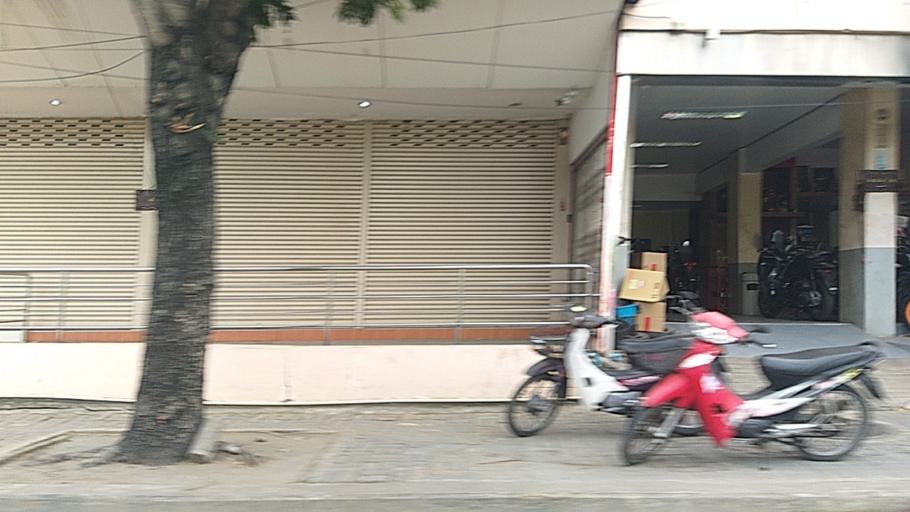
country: TH
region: Bangkok
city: Bang Na
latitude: 13.6807
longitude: 100.6644
